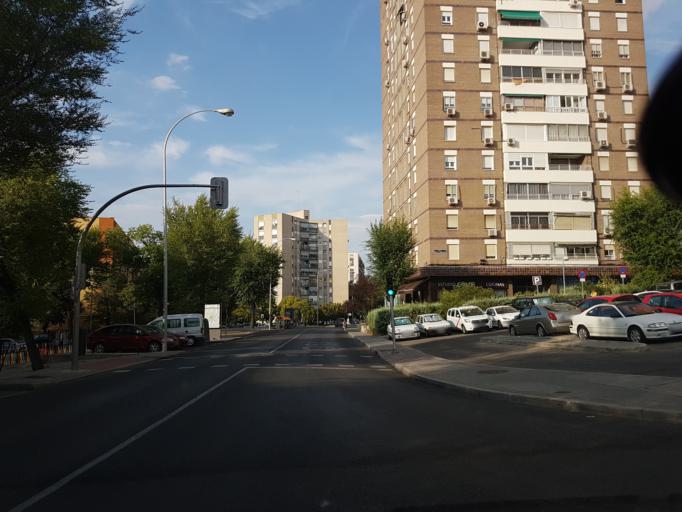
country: ES
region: Madrid
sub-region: Provincia de Madrid
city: Moratalaz
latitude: 40.4090
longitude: -3.6570
